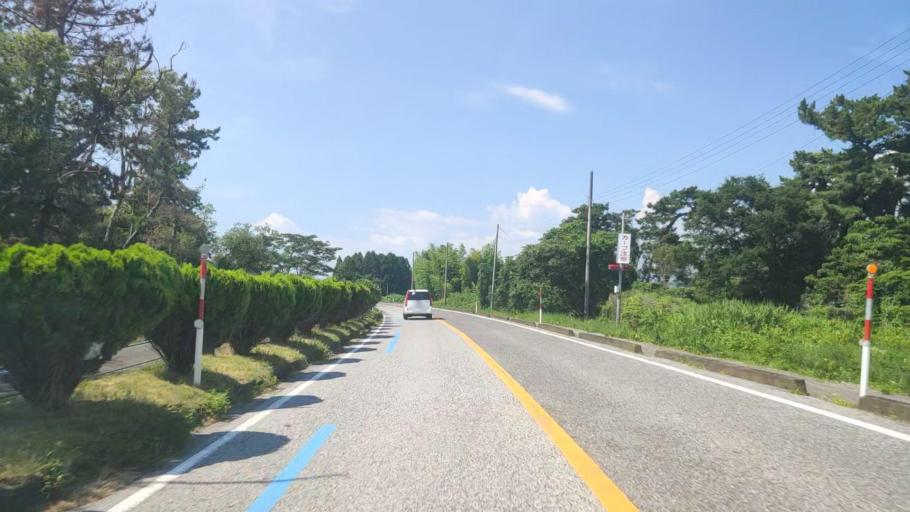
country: JP
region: Shiga Prefecture
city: Nagahama
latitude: 35.3969
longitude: 136.2180
